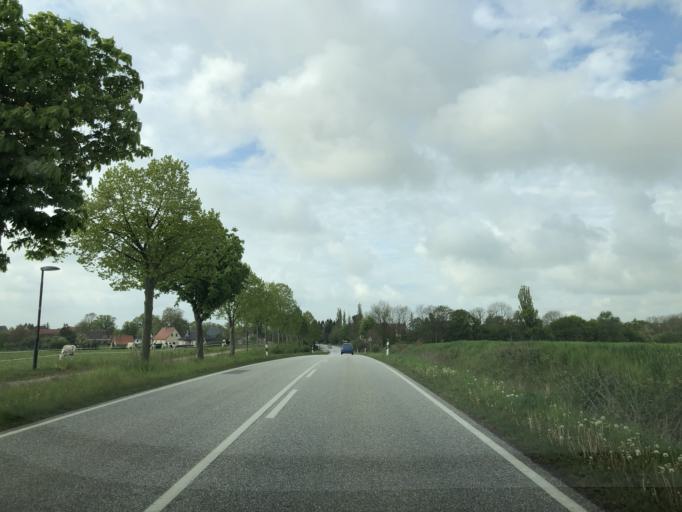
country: DE
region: Mecklenburg-Vorpommern
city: Goldberg
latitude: 53.5773
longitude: 12.0809
